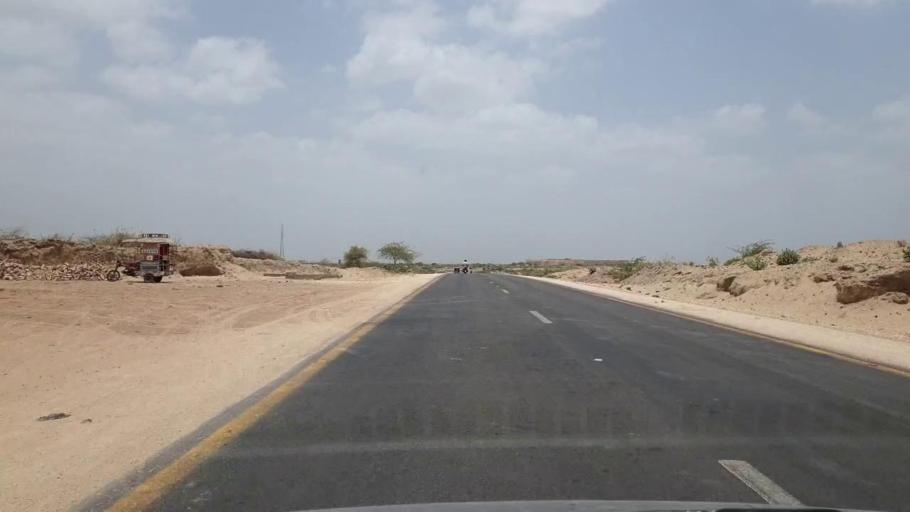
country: PK
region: Sindh
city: Naukot
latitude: 24.8401
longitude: 69.4584
